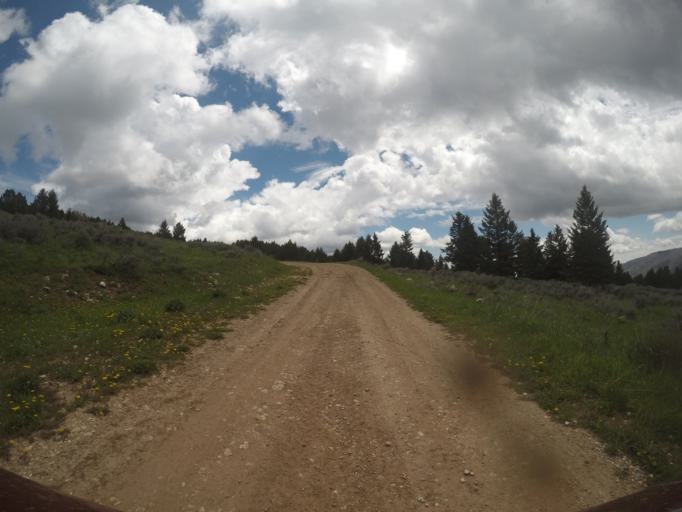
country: US
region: Wyoming
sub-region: Big Horn County
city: Lovell
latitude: 45.1684
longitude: -108.4243
